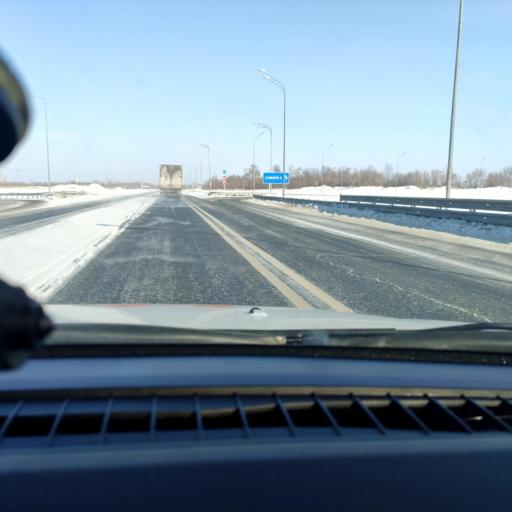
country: RU
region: Samara
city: Smyshlyayevka
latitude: 53.1490
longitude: 50.3934
